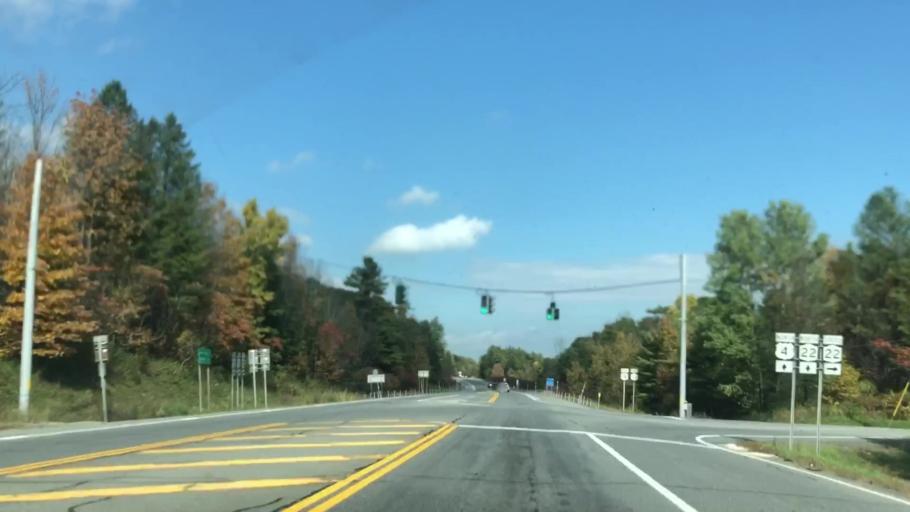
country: US
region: New York
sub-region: Washington County
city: Whitehall
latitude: 43.4573
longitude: -73.4453
